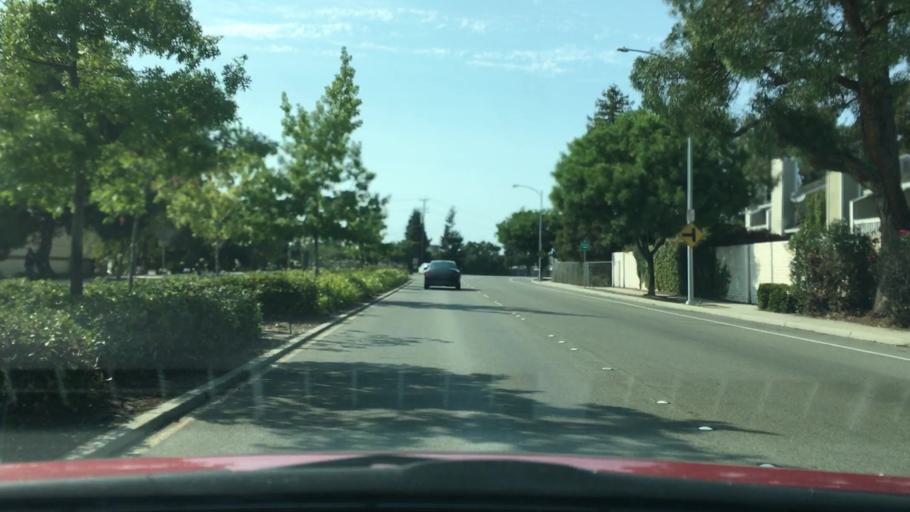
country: US
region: California
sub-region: Santa Clara County
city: Milpitas
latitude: 37.4454
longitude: -121.9077
